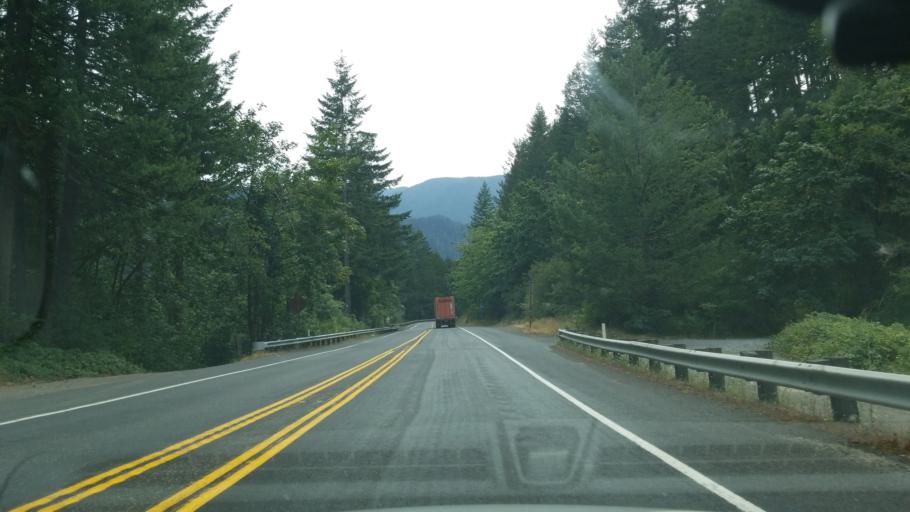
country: US
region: Oregon
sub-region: Hood River County
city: Cascade Locks
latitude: 45.6617
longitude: -121.9060
